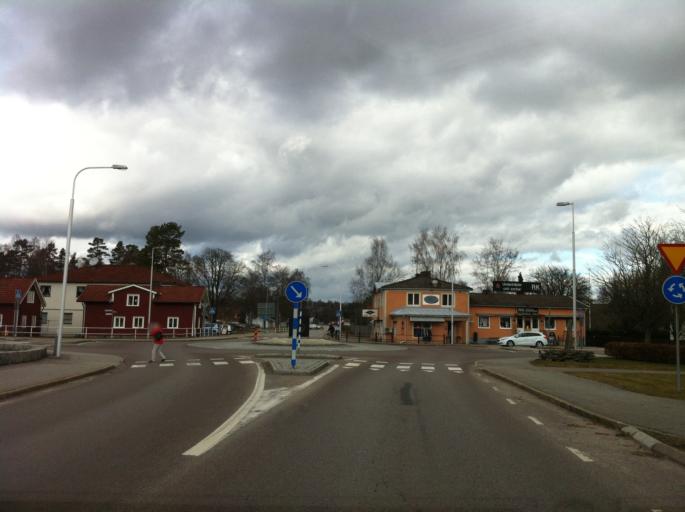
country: SE
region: Vaestra Goetaland
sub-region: Tranemo Kommun
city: Limmared
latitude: 57.6424
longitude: 13.4434
